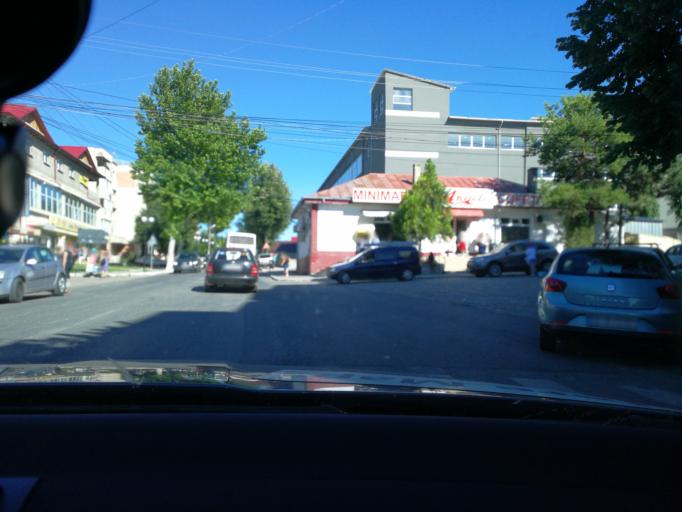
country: RO
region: Tulcea
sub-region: Oras Macin
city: Macin
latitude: 45.2445
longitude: 28.1319
